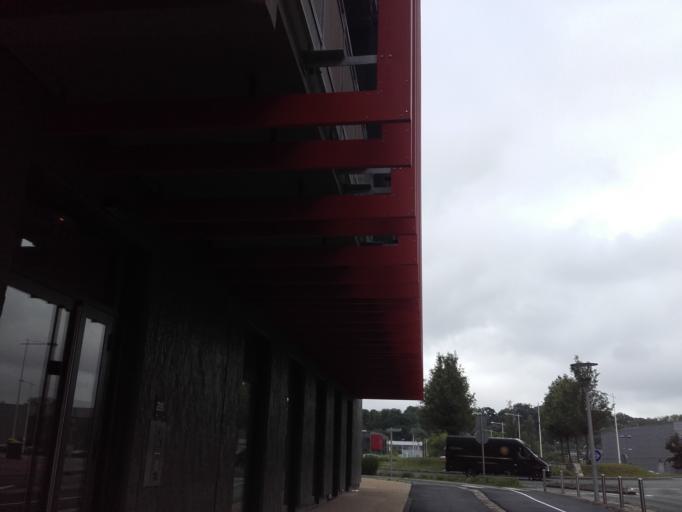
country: FR
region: Centre
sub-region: Departement d'Indre-et-Loire
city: Tours
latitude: 47.3662
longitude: 0.6807
